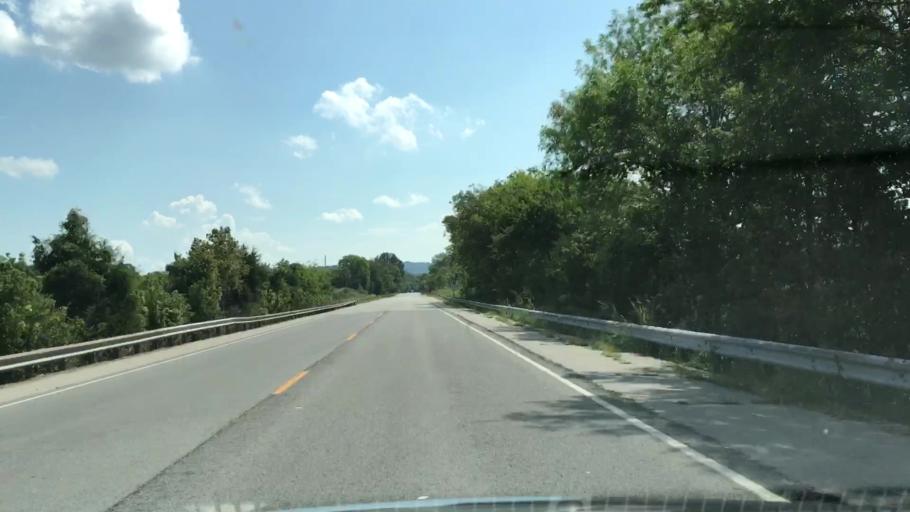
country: US
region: Tennessee
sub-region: Trousdale County
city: Hartsville
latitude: 36.3631
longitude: -86.0655
